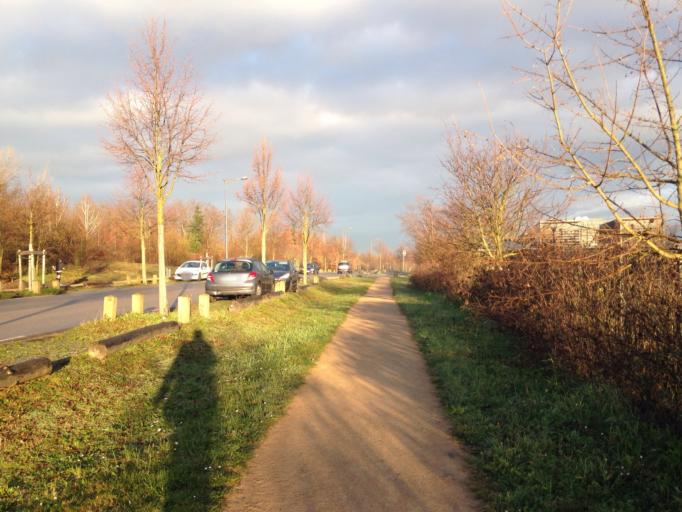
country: FR
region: Rhone-Alpes
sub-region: Departement du Rhone
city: Saint-Priest
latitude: 45.7115
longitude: 4.9281
